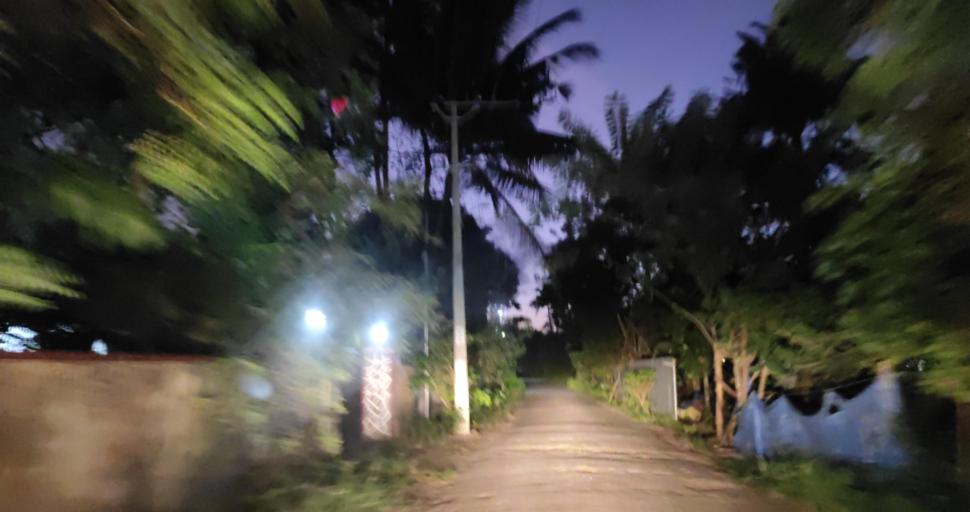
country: IN
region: Kerala
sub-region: Alappuzha
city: Shertallai
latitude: 9.6245
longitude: 76.3451
